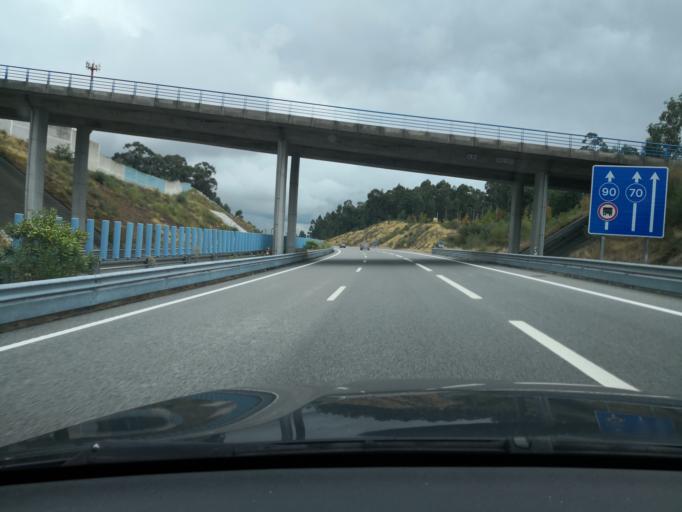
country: PT
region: Porto
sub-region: Lousada
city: Lousada
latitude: 41.2916
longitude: -8.2874
